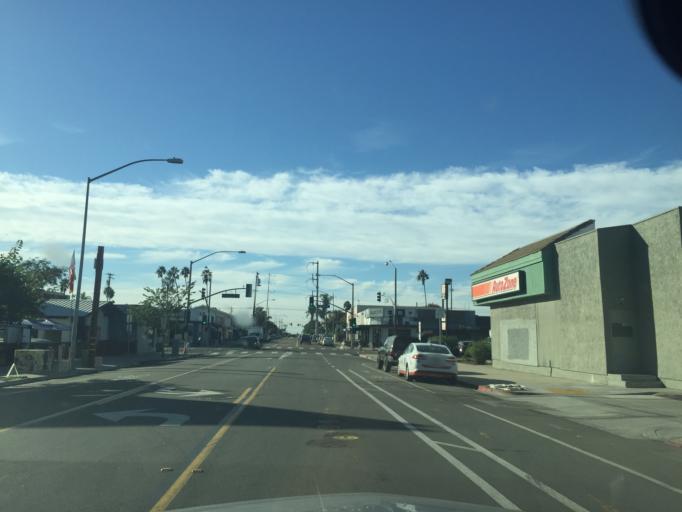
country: US
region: California
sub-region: San Diego County
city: San Diego
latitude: 32.7504
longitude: -117.1294
